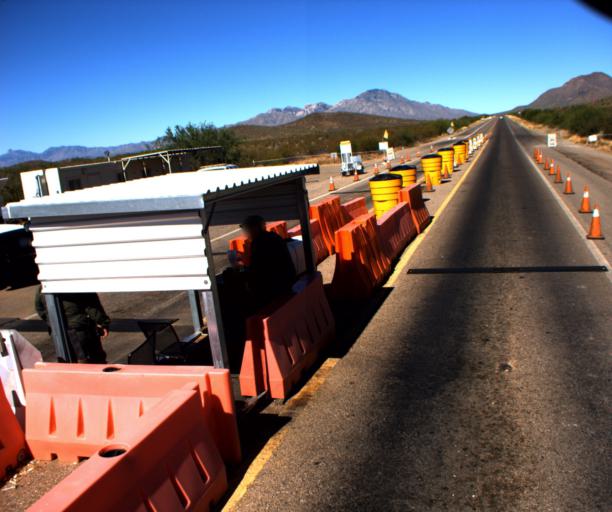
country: US
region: Arizona
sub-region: Pima County
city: Three Points
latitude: 32.0648
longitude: -111.3749
